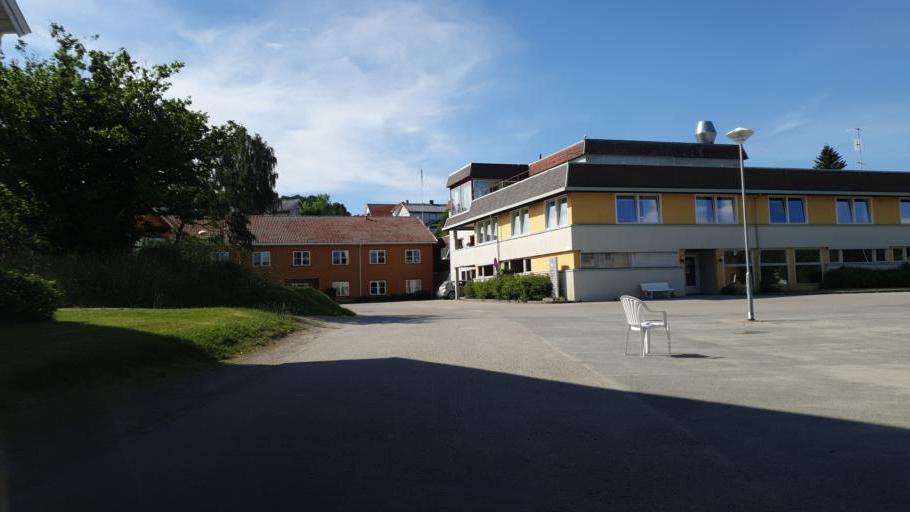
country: NO
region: Nord-Trondelag
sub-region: Leksvik
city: Leksvik
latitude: 63.6723
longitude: 10.6309
